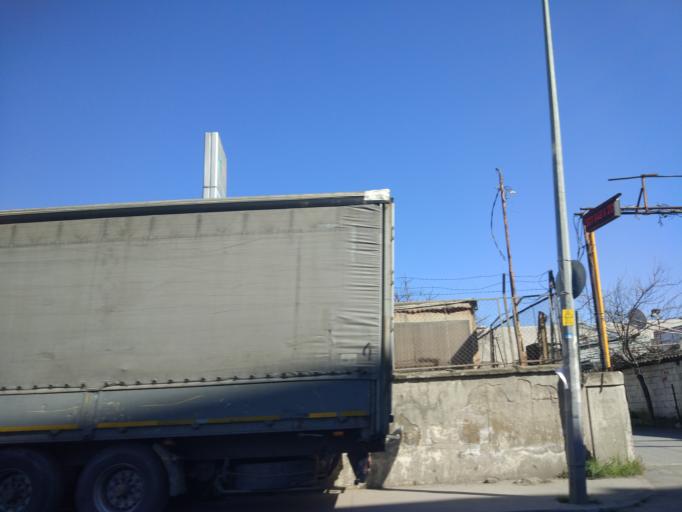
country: TR
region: Istanbul
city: Mahmutbey
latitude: 41.0239
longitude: 28.8062
